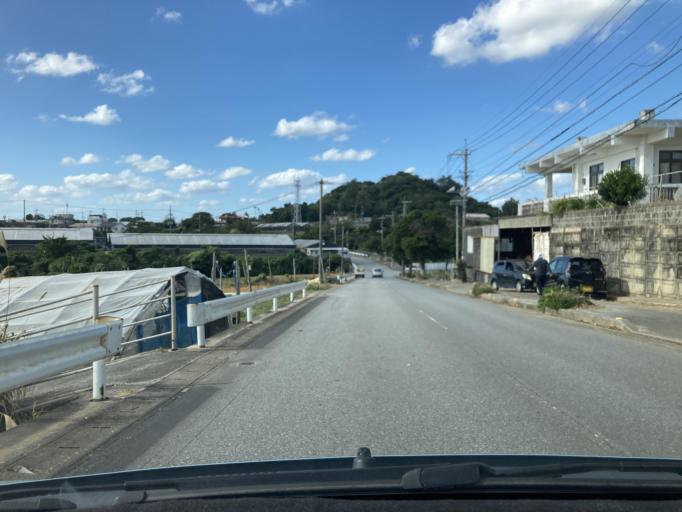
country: JP
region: Okinawa
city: Gushikawa
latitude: 26.3719
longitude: 127.8370
